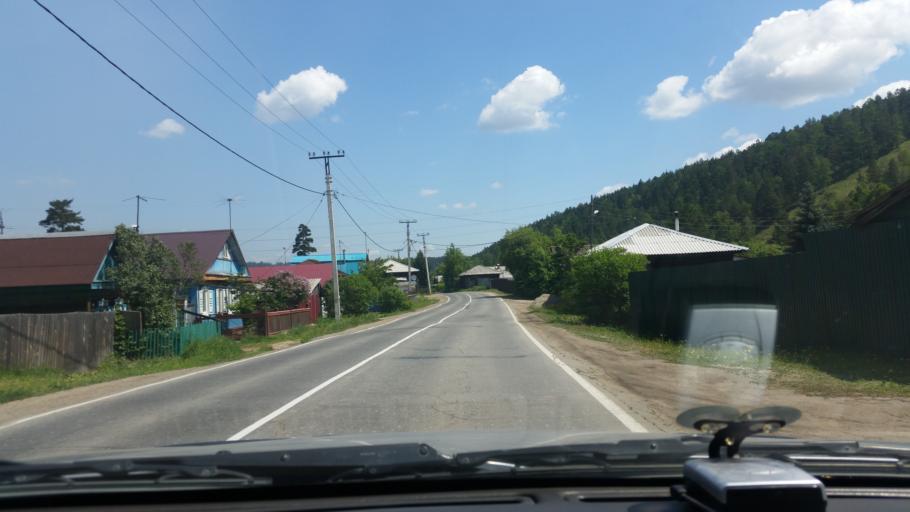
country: RU
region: Irkutsk
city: Shelekhov
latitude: 52.1544
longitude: 104.0783
